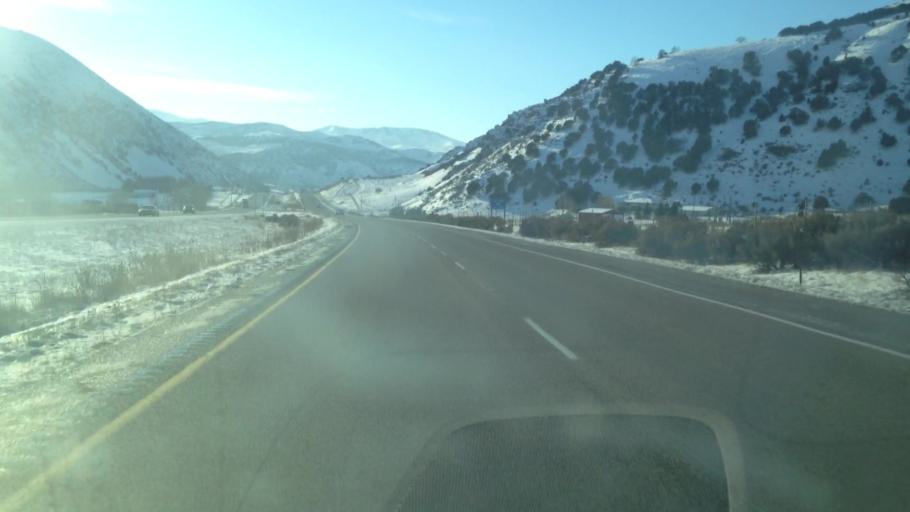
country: US
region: Idaho
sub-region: Bannock County
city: Pocatello
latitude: 42.8015
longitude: -112.3338
